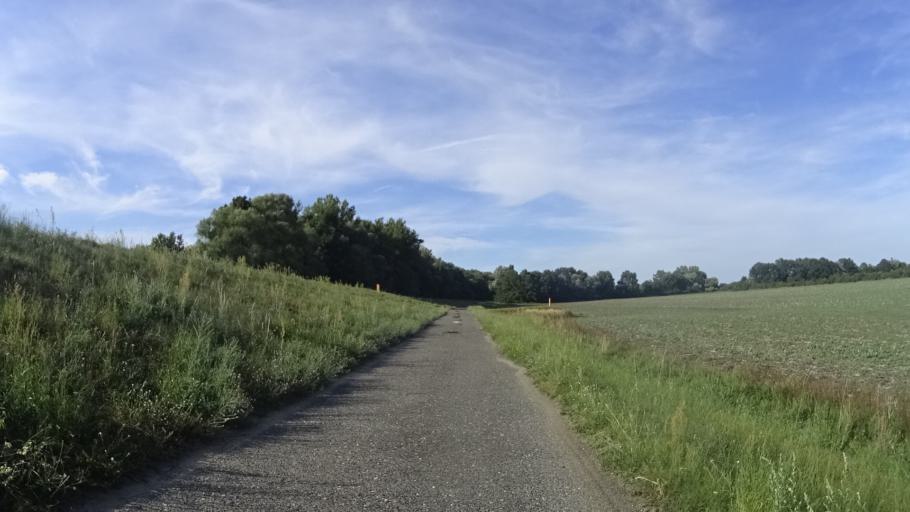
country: AT
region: Lower Austria
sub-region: Politischer Bezirk Ganserndorf
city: Drosing
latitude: 48.5348
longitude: 16.9569
